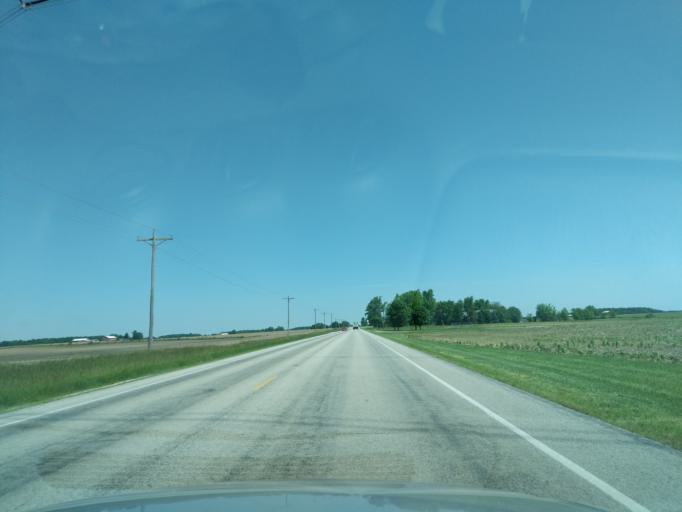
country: US
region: Indiana
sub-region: Huntington County
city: Huntington
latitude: 40.9361
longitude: -85.4710
